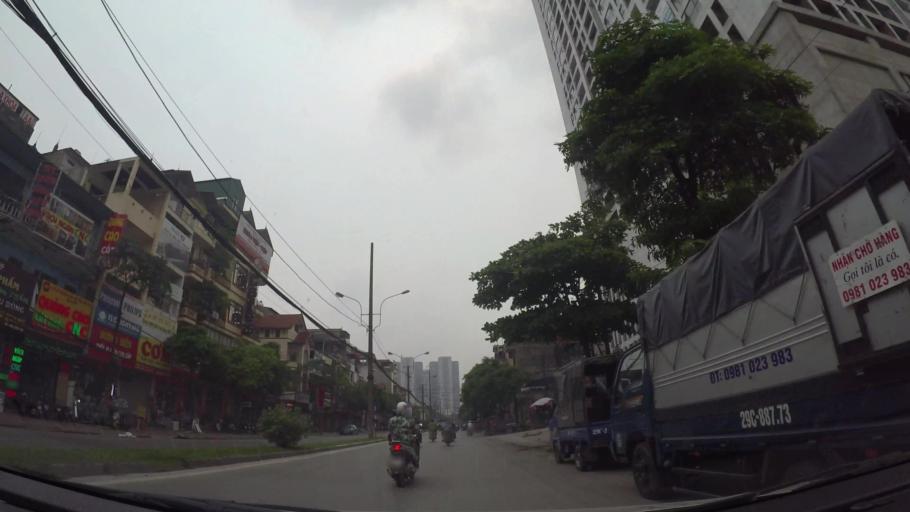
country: VN
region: Ha Noi
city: Ha Dong
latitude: 20.9818
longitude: 105.7708
